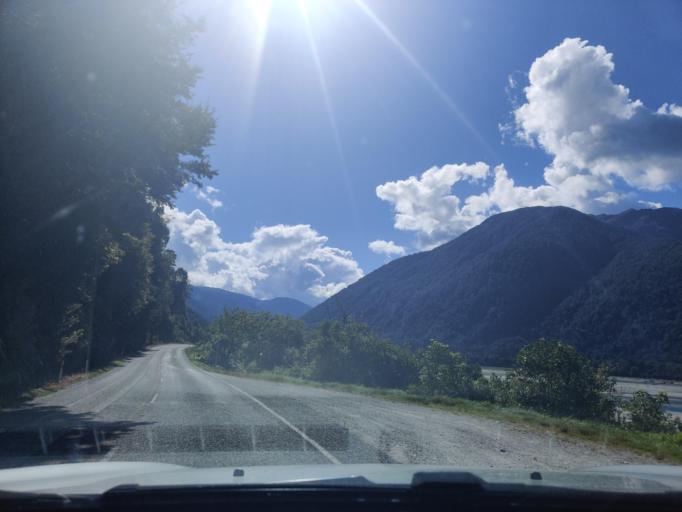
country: NZ
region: Otago
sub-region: Queenstown-Lakes District
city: Wanaka
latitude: -43.9456
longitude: 169.1475
